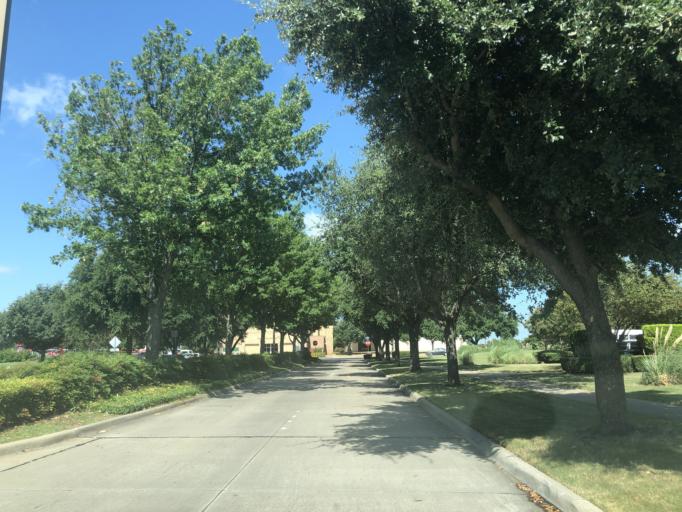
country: US
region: Texas
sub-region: Dallas County
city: Duncanville
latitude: 32.6486
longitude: -96.9073
